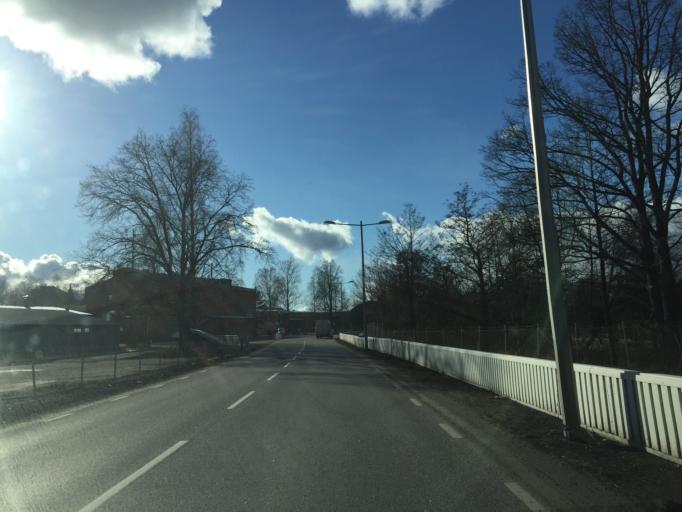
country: SE
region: OErebro
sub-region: Orebro Kommun
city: Orebro
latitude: 59.2778
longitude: 15.2376
